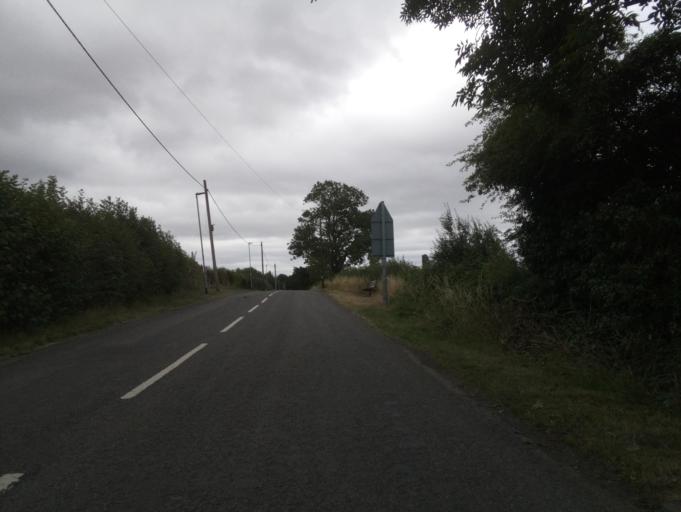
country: GB
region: England
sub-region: Leicestershire
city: Donisthorpe
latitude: 52.7249
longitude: -1.5195
